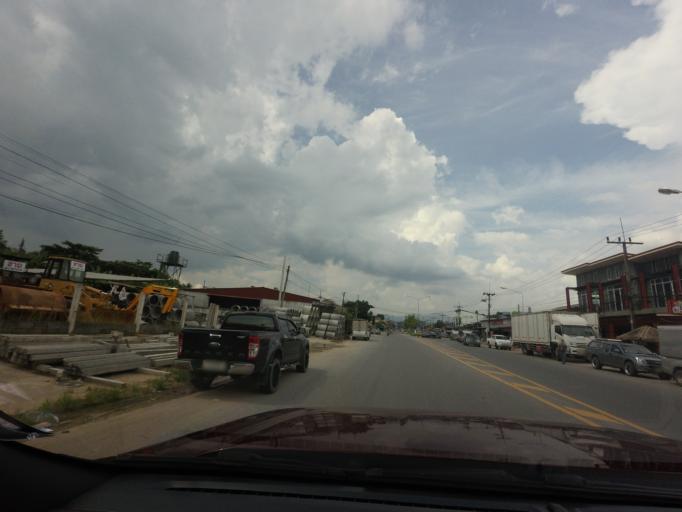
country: TH
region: Yala
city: Ban Nang Sata
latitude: 6.2603
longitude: 101.2549
